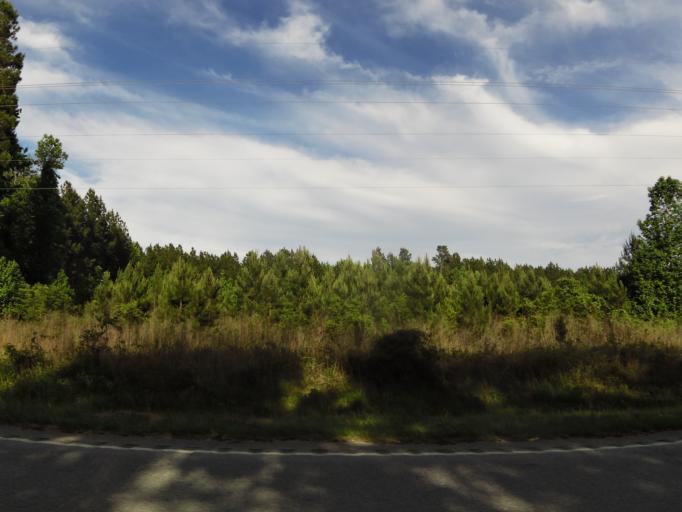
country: US
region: South Carolina
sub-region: Allendale County
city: Fairfax
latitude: 32.9135
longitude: -81.2376
